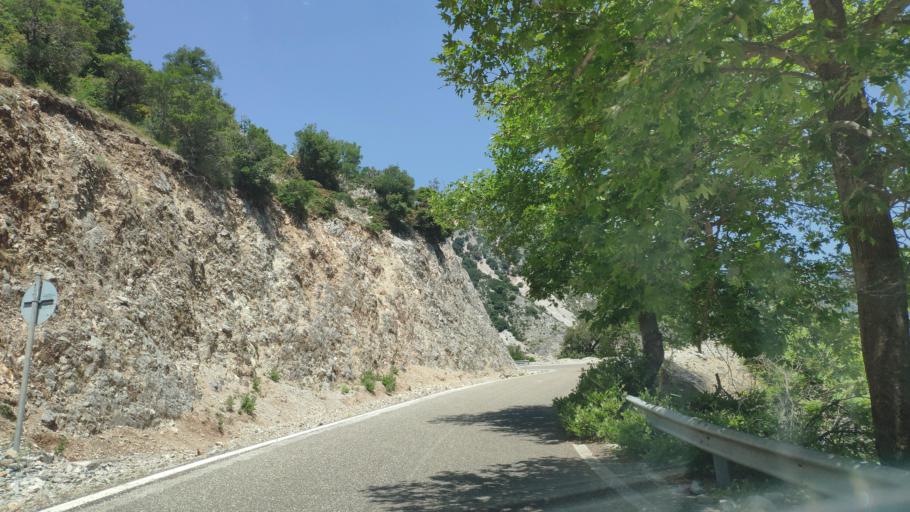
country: GR
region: West Greece
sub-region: Nomos Aitolias kai Akarnanias
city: Krikellos
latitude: 39.0137
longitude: 21.3725
